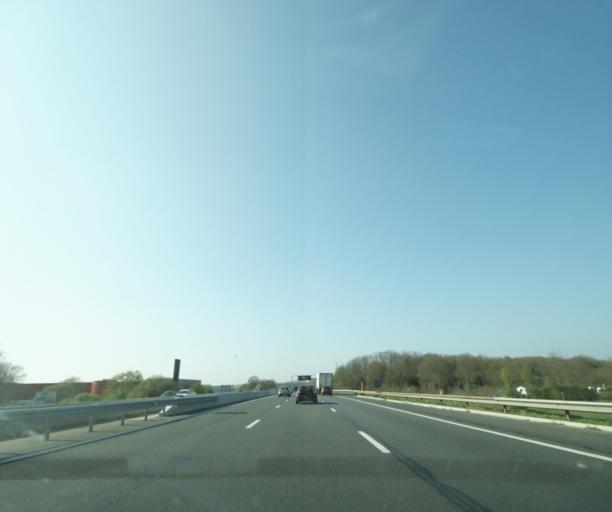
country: FR
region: Ile-de-France
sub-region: Departement de Seine-et-Marne
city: Nemours
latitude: 48.2790
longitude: 2.7057
